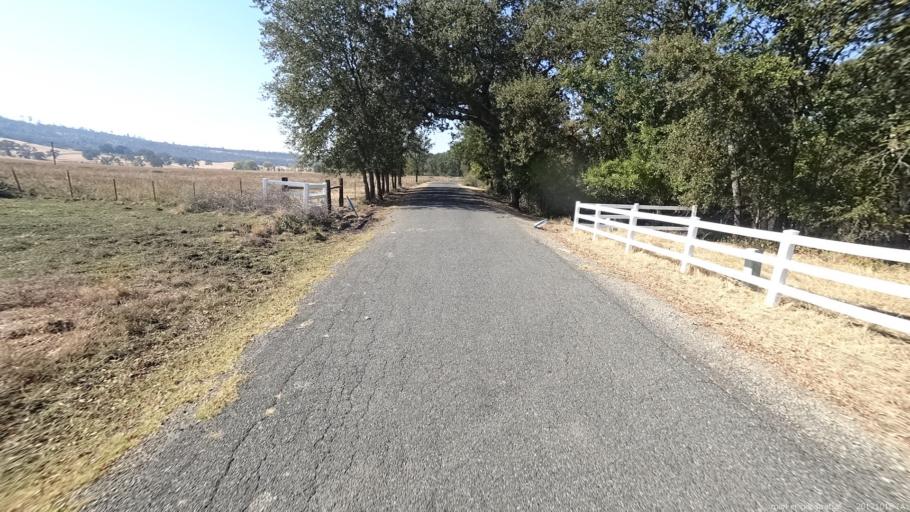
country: US
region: California
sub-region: Shasta County
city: Palo Cedro
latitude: 40.5521
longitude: -122.0699
